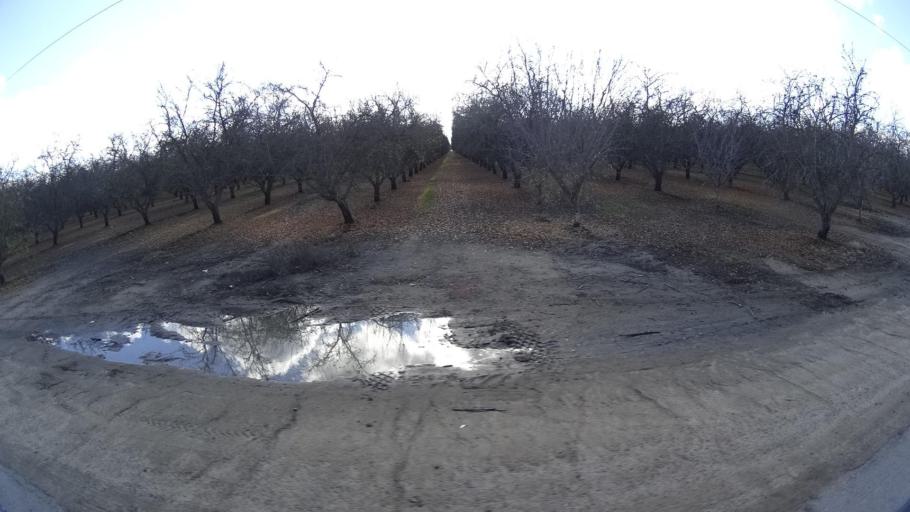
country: US
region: California
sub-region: Kern County
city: Wasco
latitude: 35.6886
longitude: -119.3277
